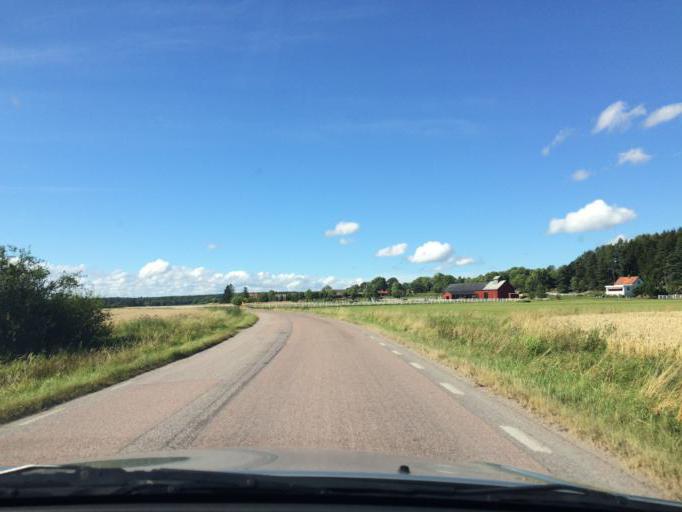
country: SE
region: Vaestmanland
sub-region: Vasteras
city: Vasteras
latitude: 59.5482
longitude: 16.4526
